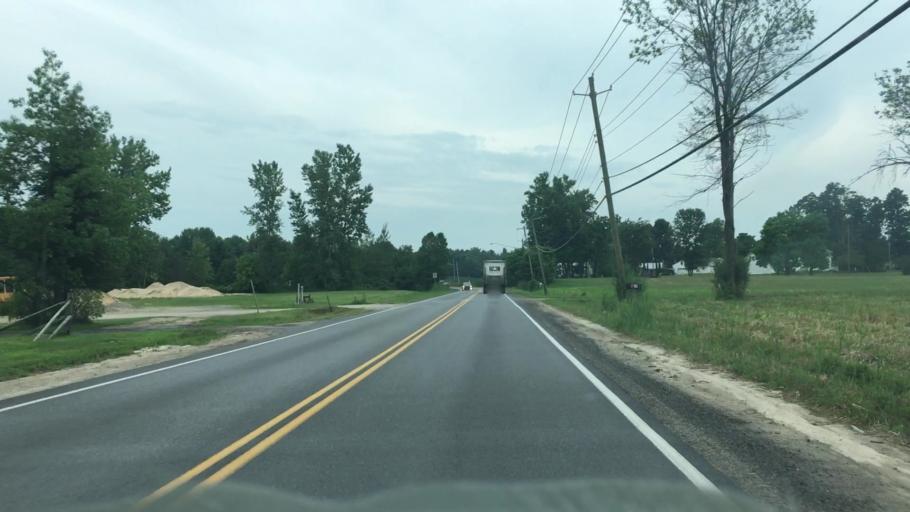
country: US
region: New York
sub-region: Clinton County
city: Plattsburgh West
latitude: 44.6730
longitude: -73.5066
